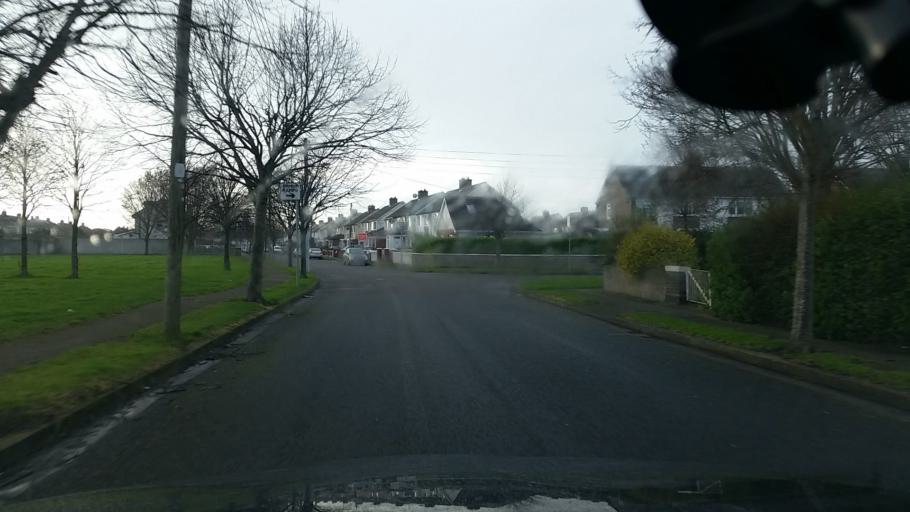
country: IE
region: Leinster
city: Artane
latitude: 53.3893
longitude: -6.2084
